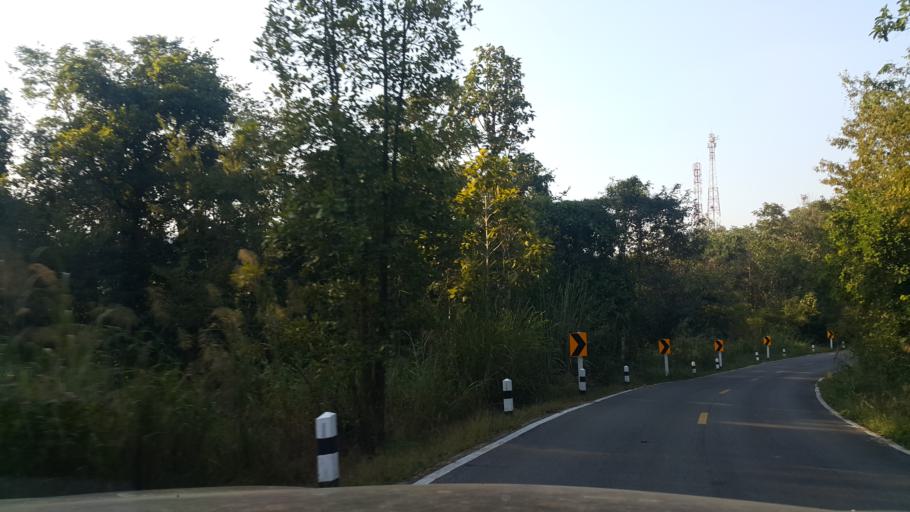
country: TH
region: Lampang
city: Hang Chat
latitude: 18.3529
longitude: 99.2480
